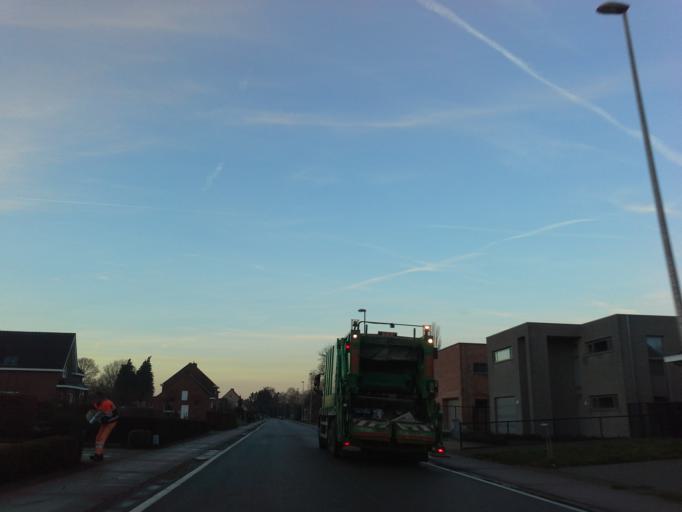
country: BE
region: Flanders
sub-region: Provincie Limburg
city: Tessenderlo
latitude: 51.0887
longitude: 5.0513
